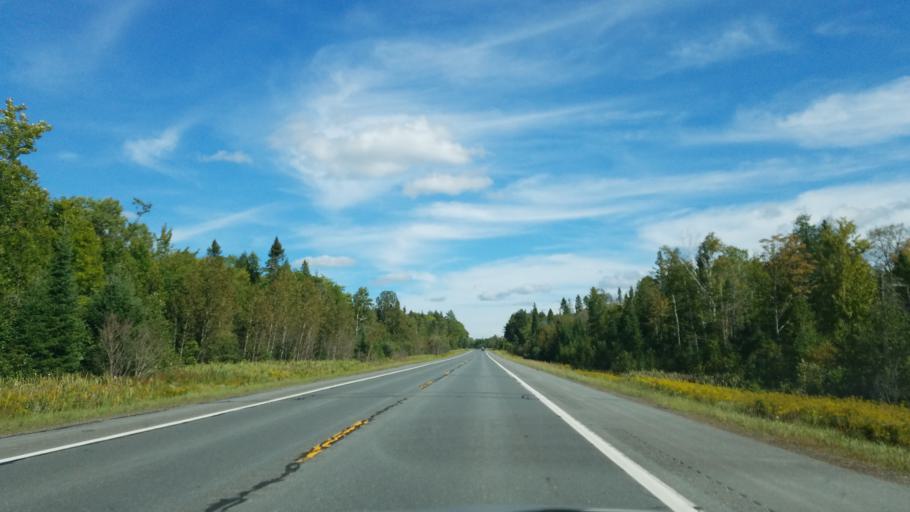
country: US
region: Michigan
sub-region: Baraga County
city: L'Anse
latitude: 46.5811
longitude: -88.4628
